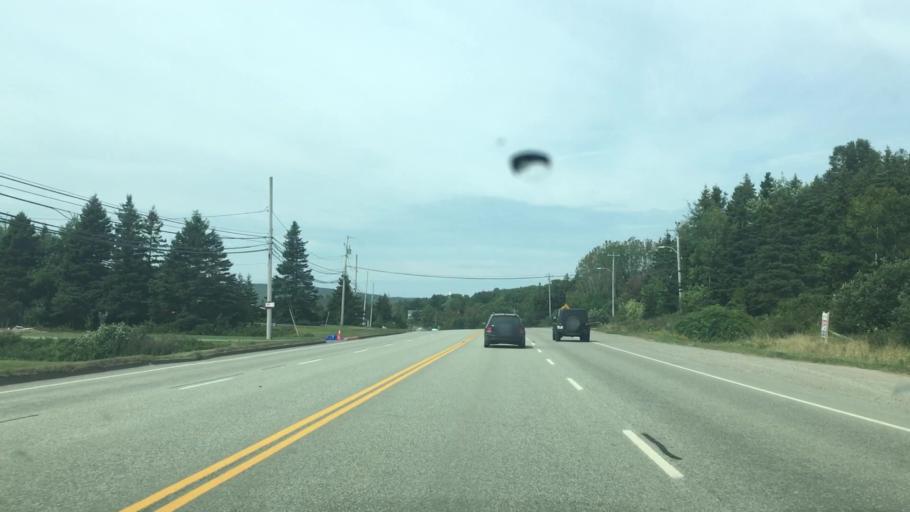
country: CA
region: Nova Scotia
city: Port Hawkesbury
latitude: 45.6421
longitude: -61.3912
